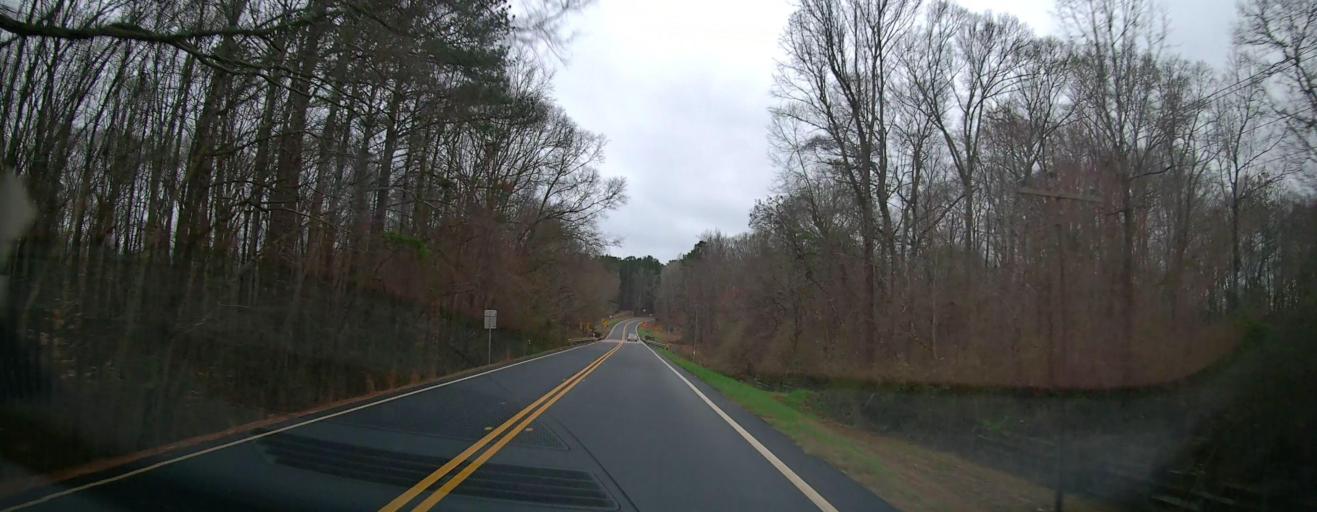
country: US
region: Georgia
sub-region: Lamar County
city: Barnesville
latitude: 33.0670
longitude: -84.2468
